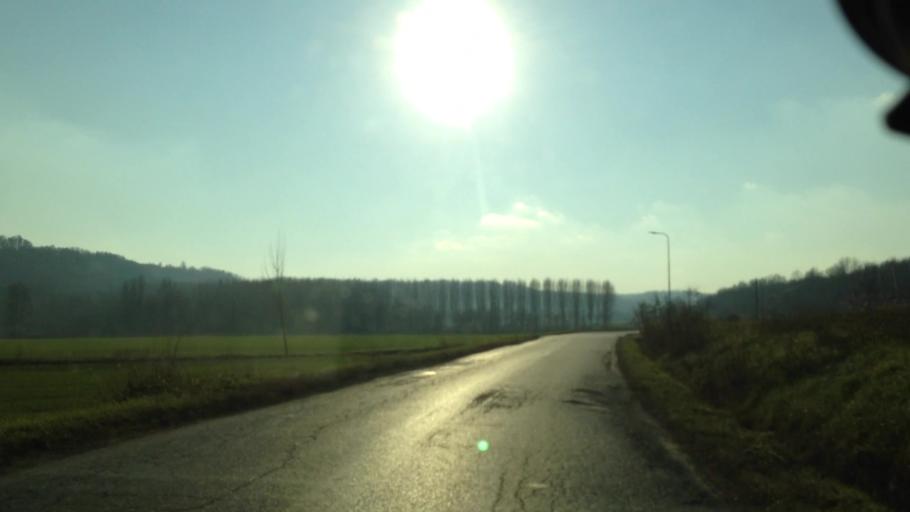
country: IT
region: Piedmont
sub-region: Provincia di Alessandria
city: Masio
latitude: 44.8469
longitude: 8.3976
